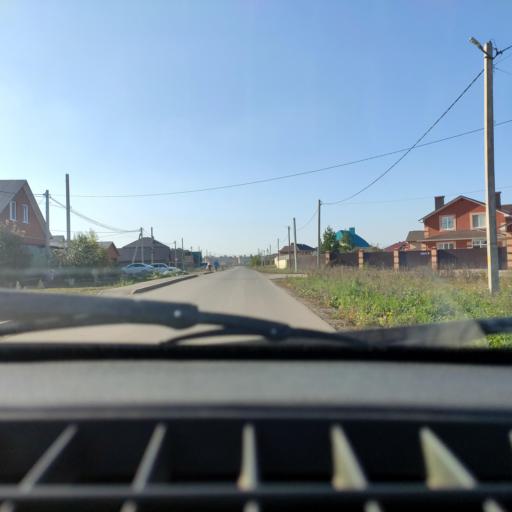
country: RU
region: Bashkortostan
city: Ufa
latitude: 54.6232
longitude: 55.9045
